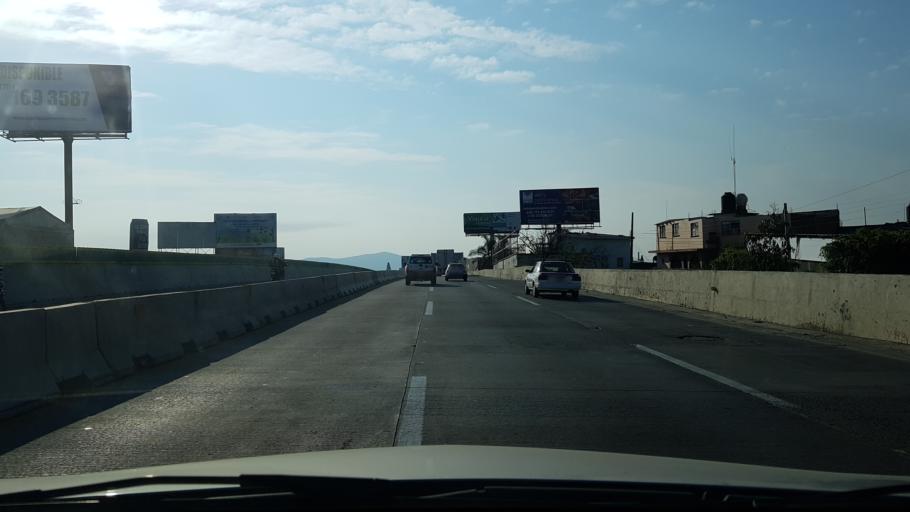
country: MX
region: Morelos
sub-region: Cuernavaca
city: Colonia los Cerritos
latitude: 18.9549
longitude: -99.1987
